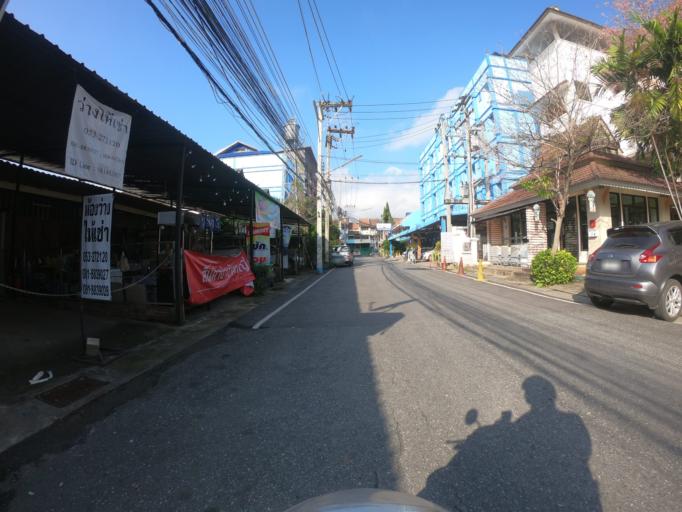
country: TH
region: Chiang Mai
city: Chiang Mai
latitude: 18.8107
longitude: 98.9663
